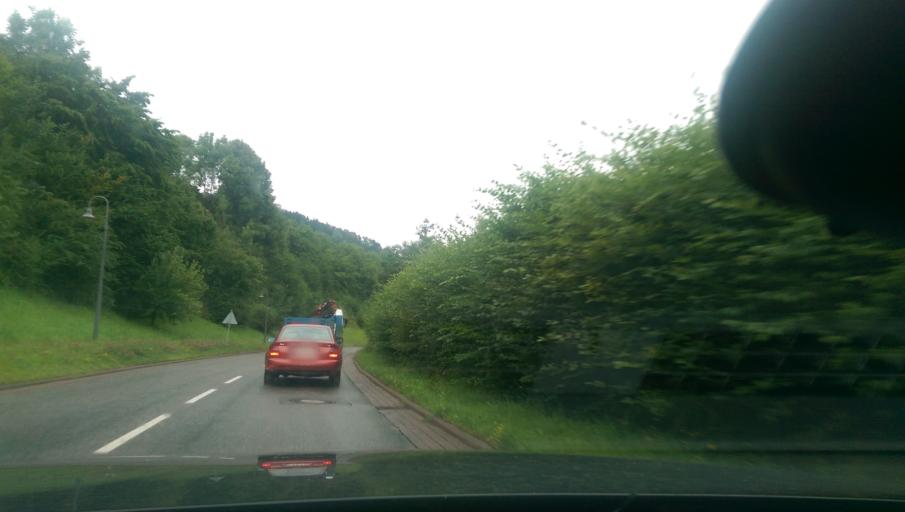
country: DE
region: Hesse
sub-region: Regierungsbezirk Kassel
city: Grossalmerode
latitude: 51.2667
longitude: 9.8328
